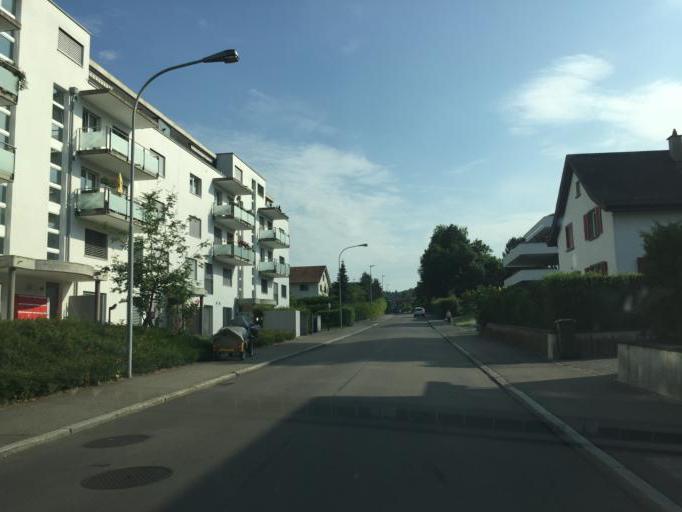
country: CH
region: Zurich
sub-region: Bezirk Buelach
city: Bulach
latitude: 47.5231
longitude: 8.5427
